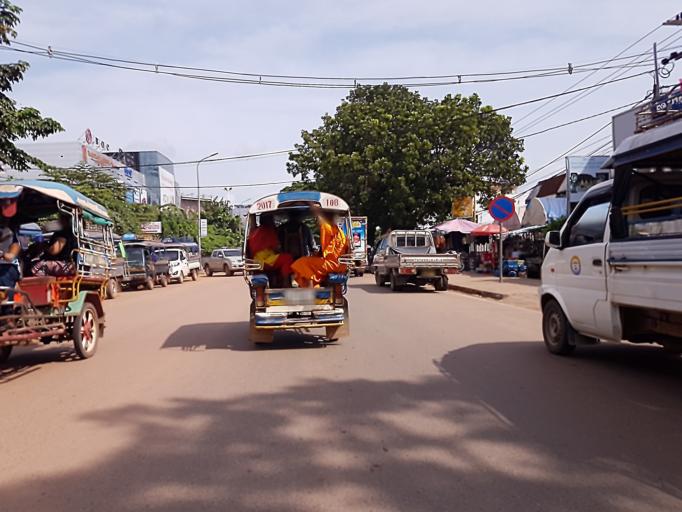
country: LA
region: Vientiane
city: Vientiane
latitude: 17.9627
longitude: 102.6161
